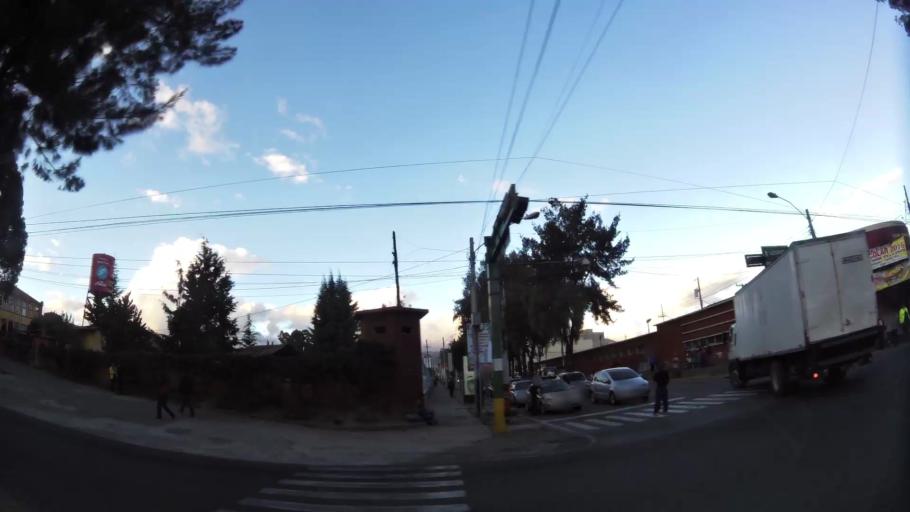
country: GT
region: Quetzaltenango
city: Quetzaltenango
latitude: 14.8446
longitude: -91.5232
